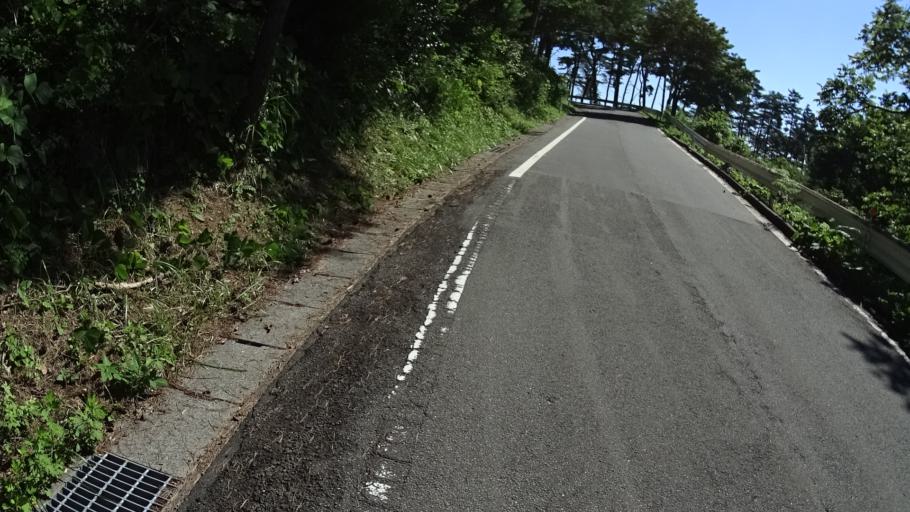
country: JP
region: Iwate
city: Ofunato
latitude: 38.8729
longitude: 141.6233
